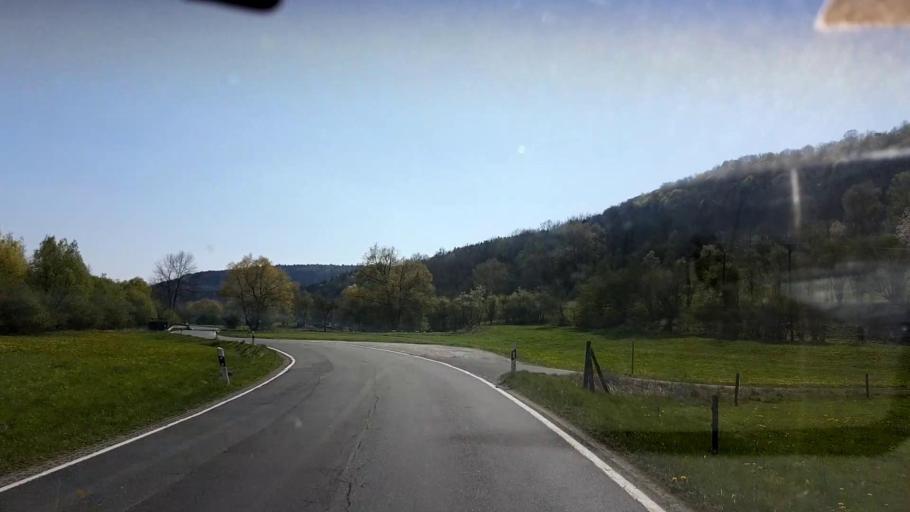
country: DE
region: Bavaria
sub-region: Upper Franconia
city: Unterleinleiter
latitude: 49.8191
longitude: 11.1928
